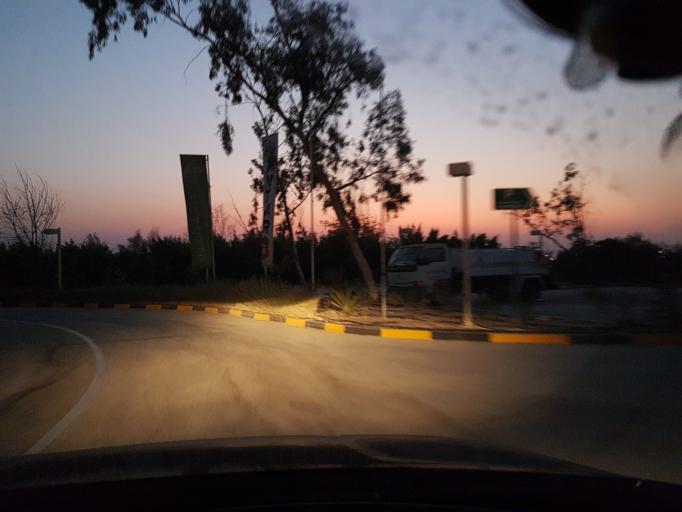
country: BH
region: Central Governorate
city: Dar Kulayb
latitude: 26.0157
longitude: 50.5088
